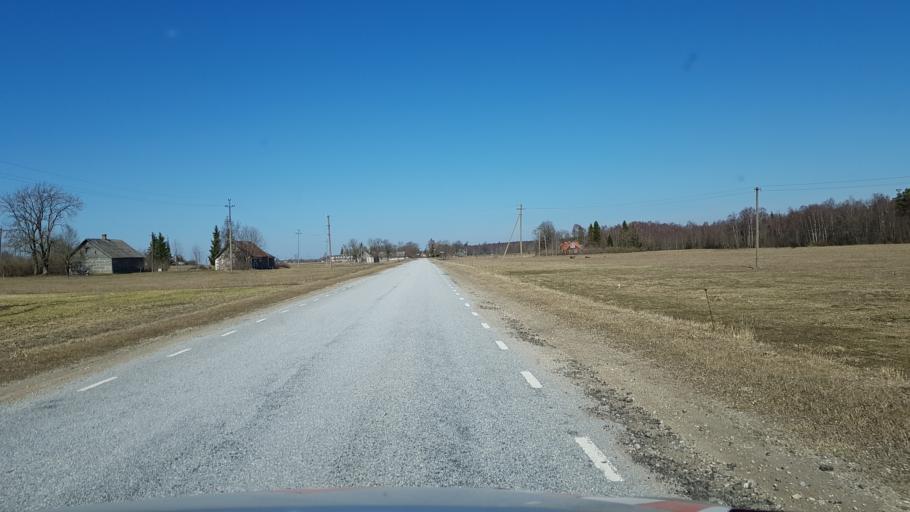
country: EE
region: Jaervamaa
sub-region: Koeru vald
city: Koeru
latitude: 59.0441
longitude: 26.0906
